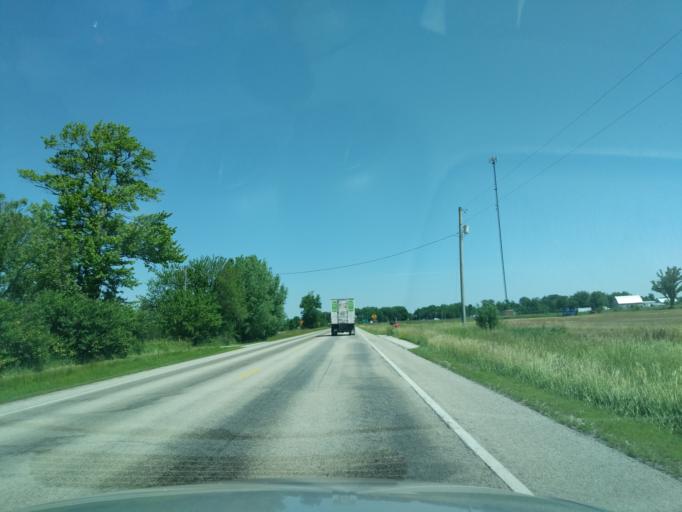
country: US
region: Indiana
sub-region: Huntington County
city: Roanoke
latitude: 40.9991
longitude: -85.4718
